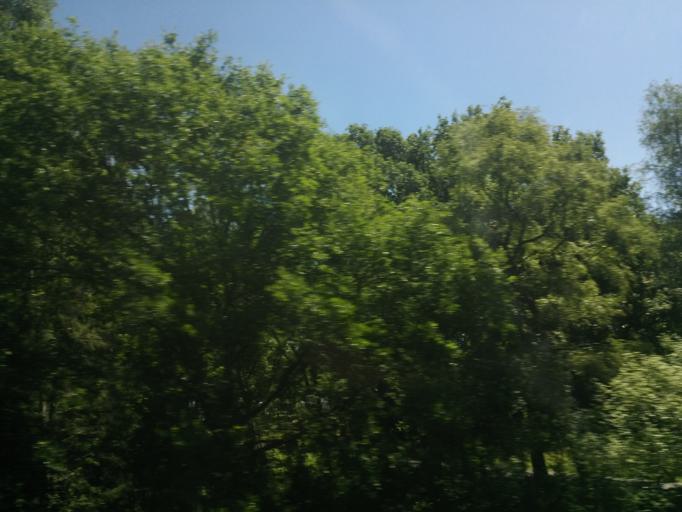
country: NL
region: Drenthe
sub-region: Gemeente Assen
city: Assen
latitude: 52.9792
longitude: 6.5664
